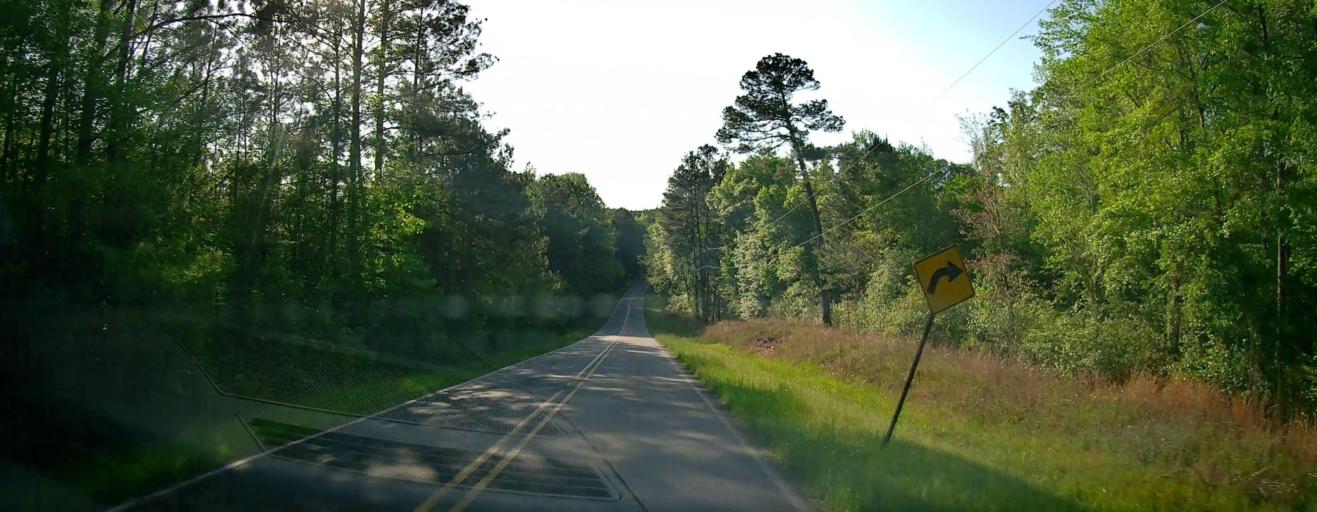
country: US
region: Georgia
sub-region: Putnam County
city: Eatonton
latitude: 33.2838
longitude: -83.3206
